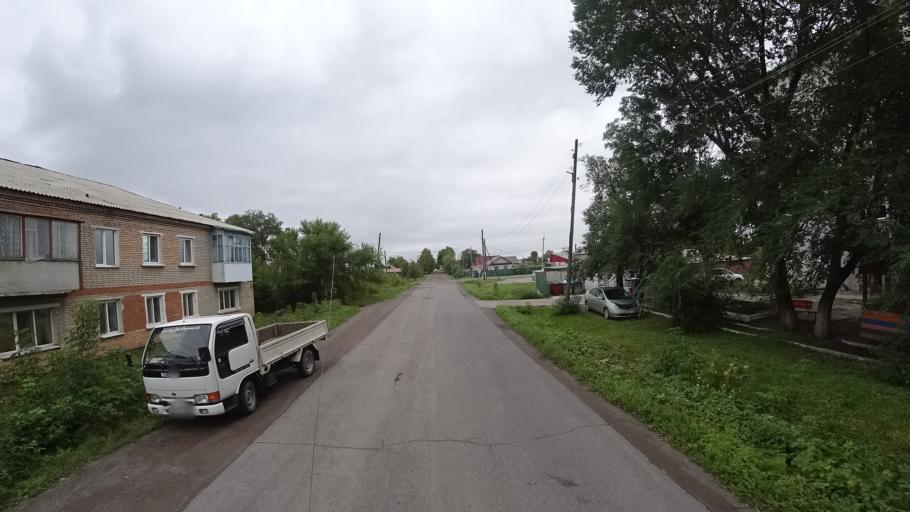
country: RU
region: Primorskiy
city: Chernigovka
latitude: 44.3475
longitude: 132.5711
